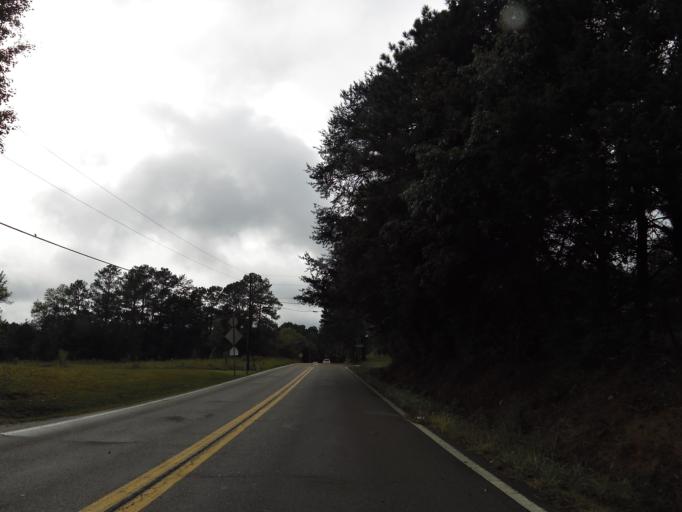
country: US
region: Tennessee
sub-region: Bradley County
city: Cleveland
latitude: 35.1775
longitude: -84.9217
